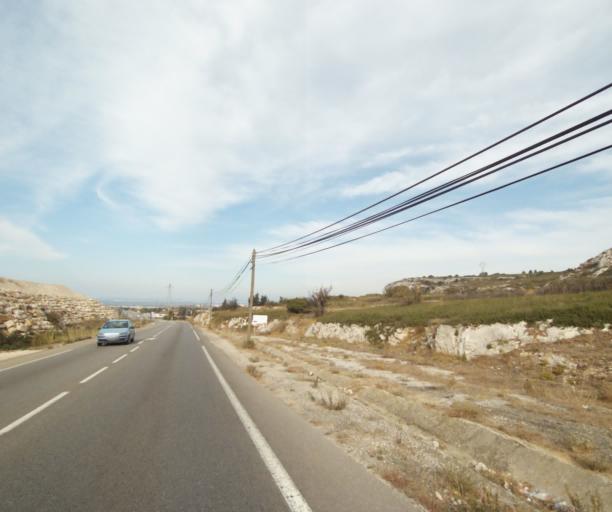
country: FR
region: Provence-Alpes-Cote d'Azur
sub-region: Departement des Bouches-du-Rhone
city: Gignac-la-Nerthe
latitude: 43.3746
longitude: 5.2284
